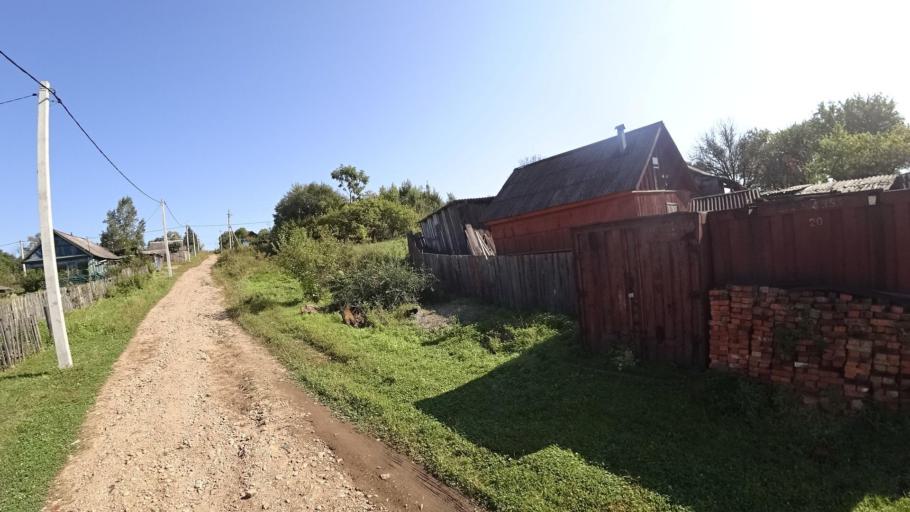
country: RU
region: Jewish Autonomous Oblast
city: Bira
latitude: 49.0063
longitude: 132.4672
